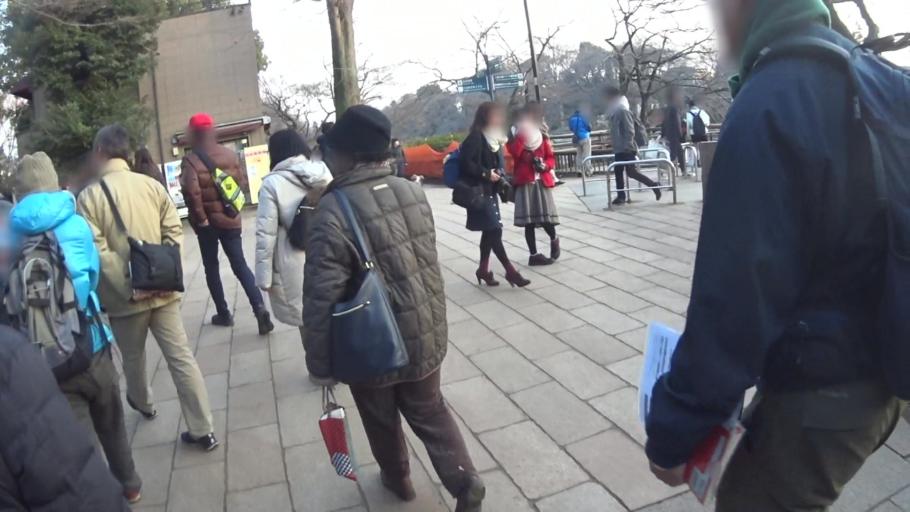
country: JP
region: Tokyo
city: Musashino
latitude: 35.7001
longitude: 139.5781
